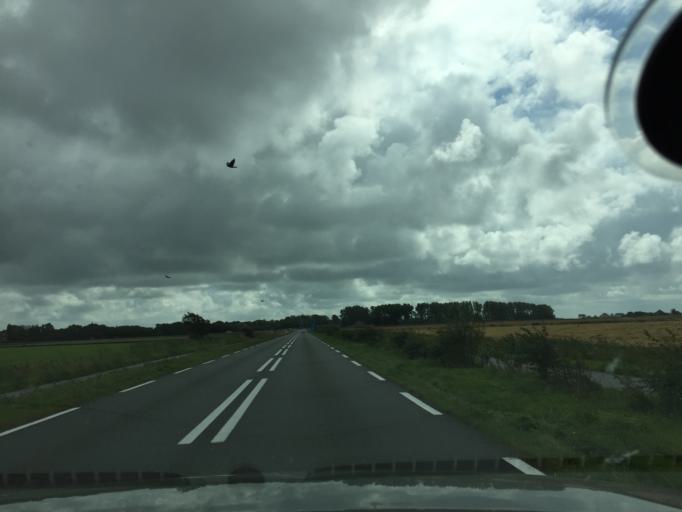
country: NL
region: North Holland
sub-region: Gemeente Texel
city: Den Burg
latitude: 53.0613
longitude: 4.7794
